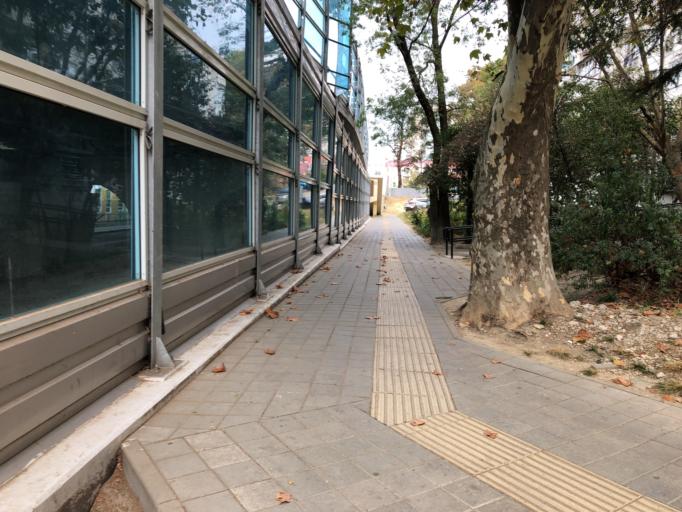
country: RU
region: Krasnodarskiy
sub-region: Sochi City
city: Sochi
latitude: 43.5933
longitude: 39.7312
